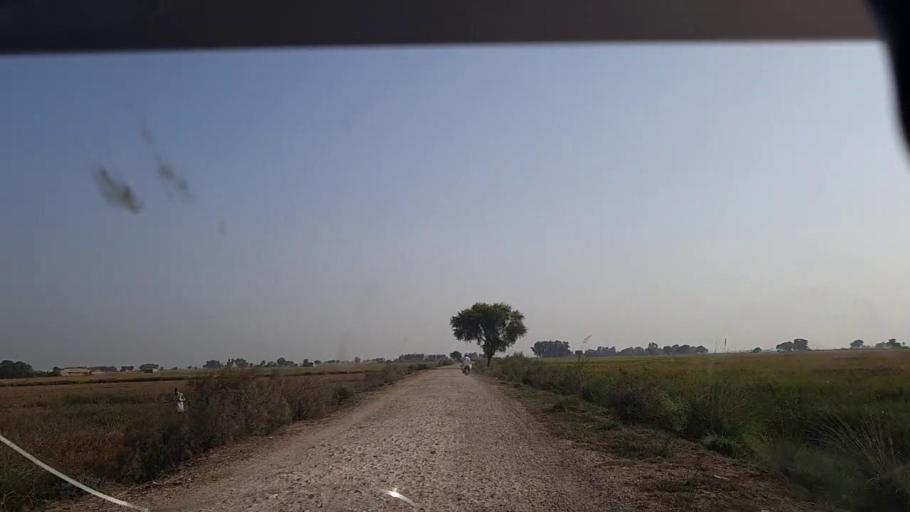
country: PK
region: Sindh
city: Shikarpur
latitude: 28.0691
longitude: 68.5460
